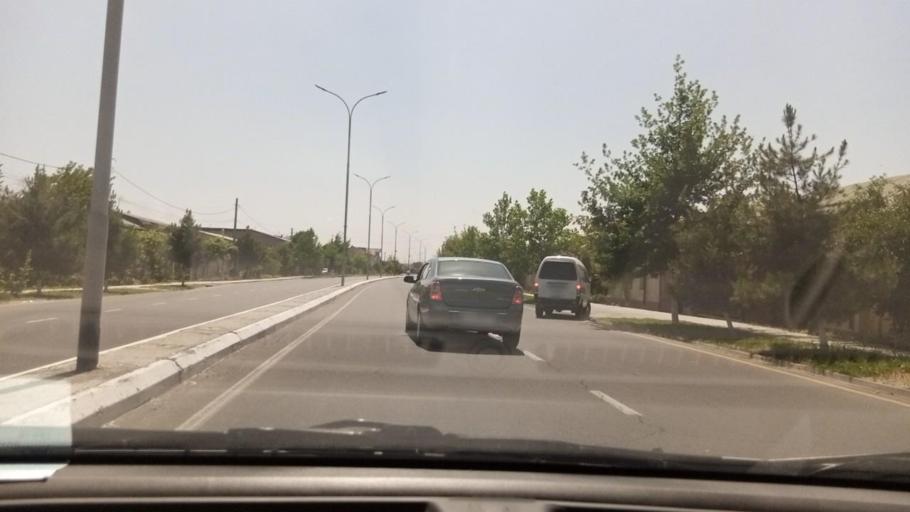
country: UZ
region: Toshkent
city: Urtaowul
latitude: 41.2041
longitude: 69.1642
